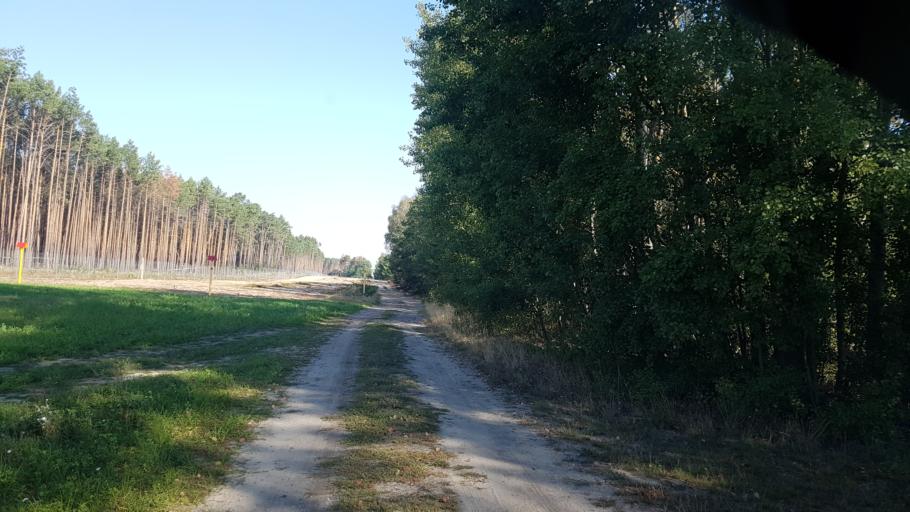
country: DE
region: Brandenburg
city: Finsterwalde
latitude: 51.6486
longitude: 13.6703
